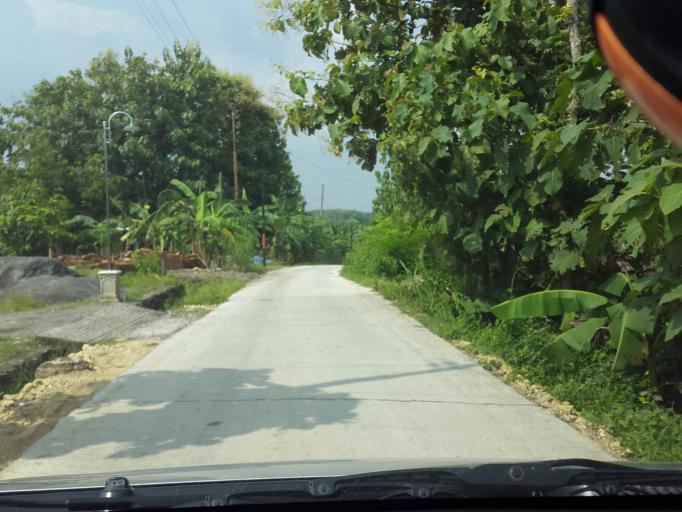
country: ID
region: Central Java
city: Sragen
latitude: -7.2858
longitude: 110.9176
